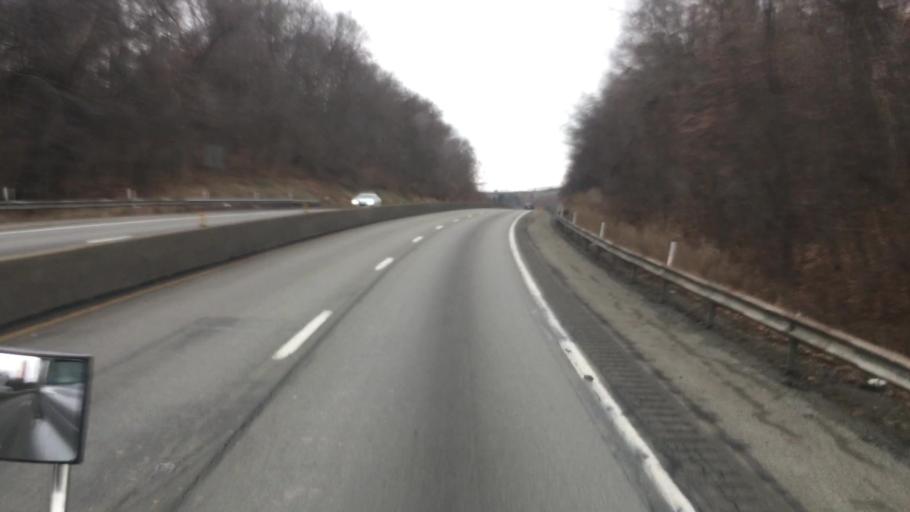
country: US
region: Pennsylvania
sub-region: Westmoreland County
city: West Newton
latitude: 40.1913
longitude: -79.6903
